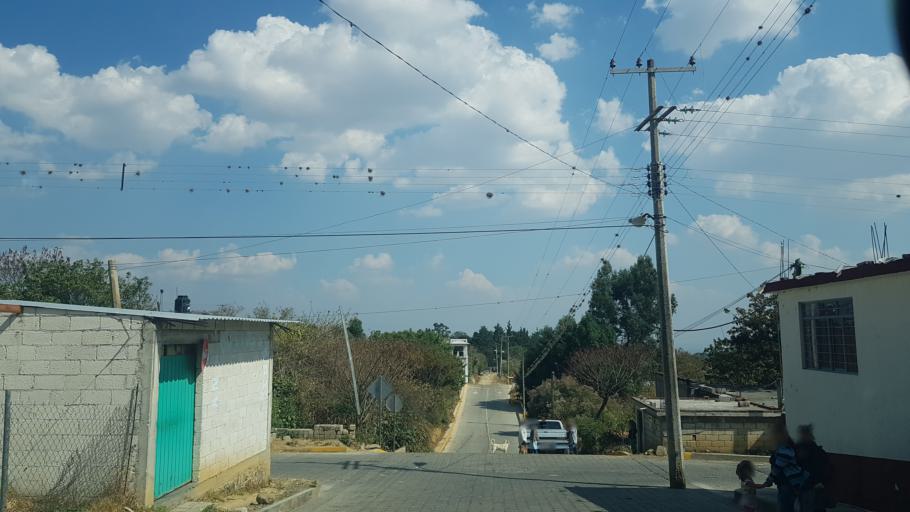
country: MX
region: Puebla
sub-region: Atlixco
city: Colonia Agricola de Ocotepec (Colonia San Jose)
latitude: 18.9267
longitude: -98.5427
